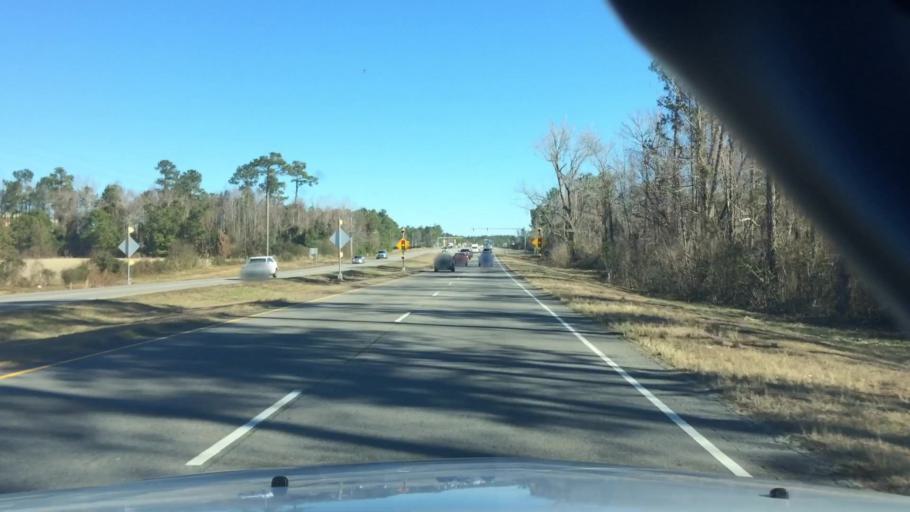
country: US
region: North Carolina
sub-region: Brunswick County
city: Bolivia
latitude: 34.0271
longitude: -78.2604
